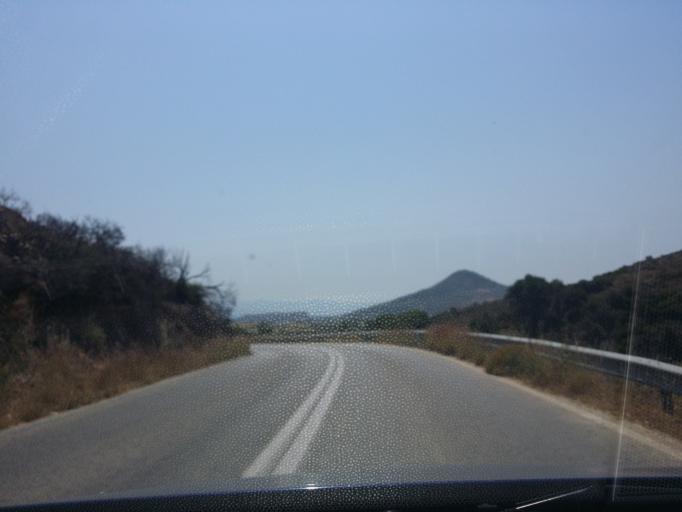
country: GR
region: South Aegean
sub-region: Nomos Kykladon
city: Naousa
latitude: 37.0628
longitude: 25.2356
